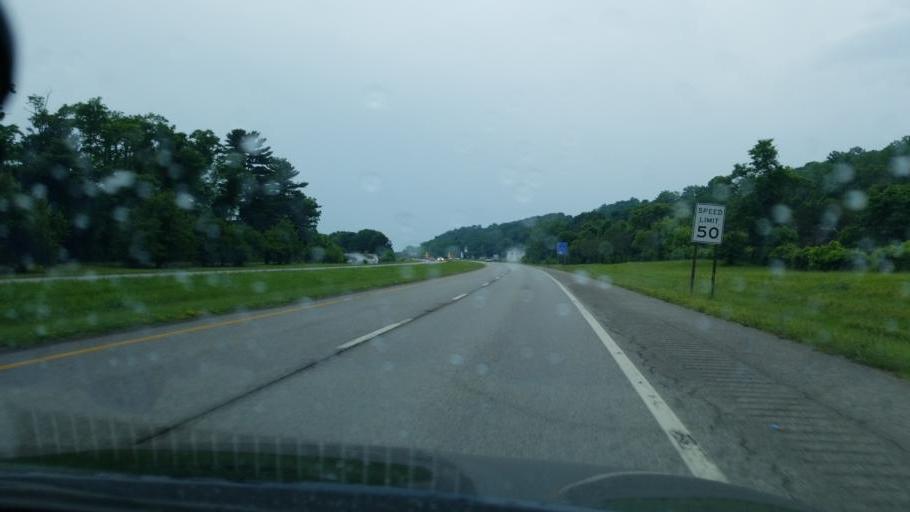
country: US
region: Ohio
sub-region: Washington County
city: Belpre
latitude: 39.2855
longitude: -81.6018
